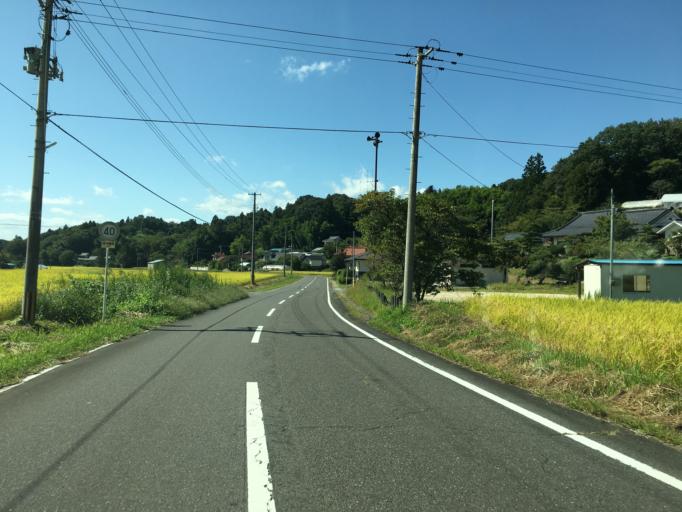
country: JP
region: Fukushima
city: Sukagawa
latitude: 37.2830
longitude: 140.4486
